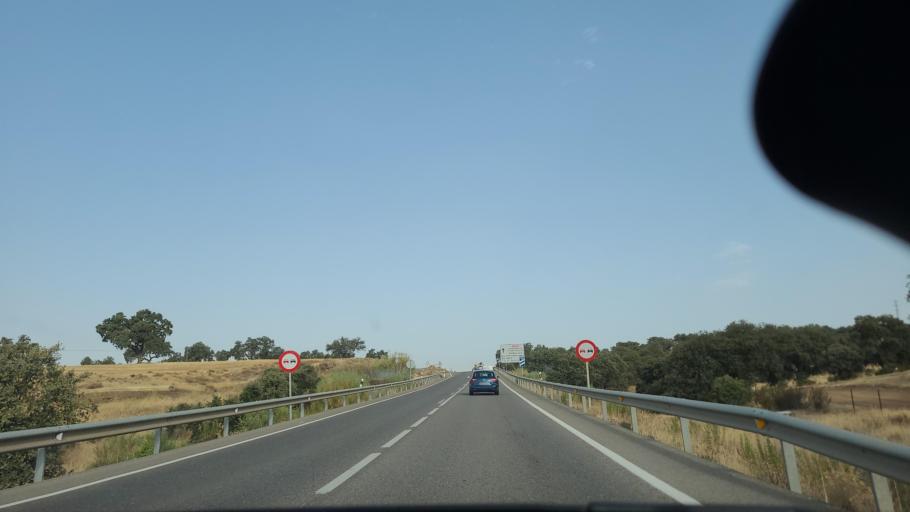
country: ES
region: Andalusia
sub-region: Province of Cordoba
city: Belmez
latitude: 38.2855
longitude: -5.2166
